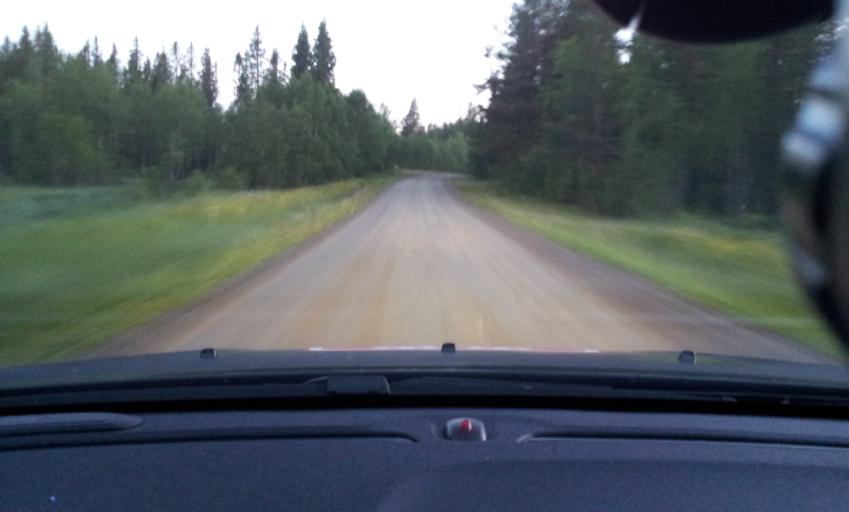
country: SE
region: Vaesternorrland
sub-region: Ange Kommun
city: Ange
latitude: 62.7680
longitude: 15.8519
